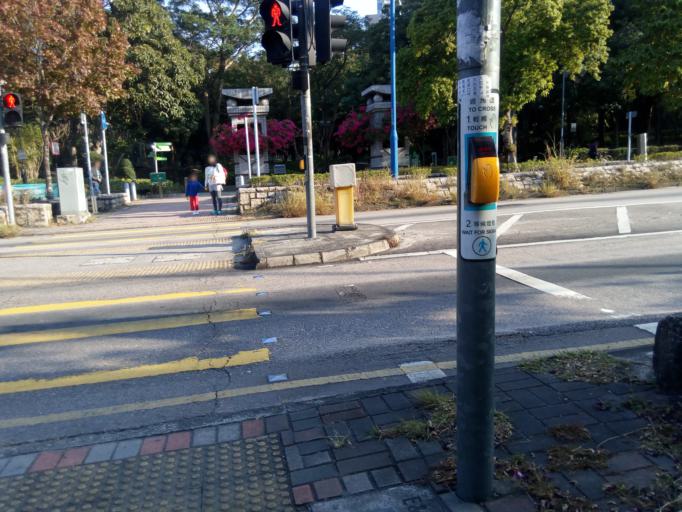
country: HK
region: Yuen Long
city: Yuen Long Kau Hui
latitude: 22.4548
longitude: 114.0022
